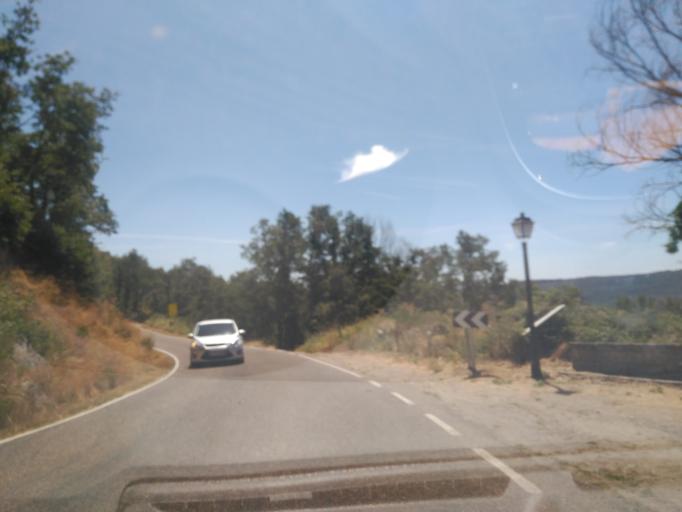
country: ES
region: Castille and Leon
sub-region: Provincia de Zamora
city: Galende
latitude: 42.1355
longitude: -6.7150
